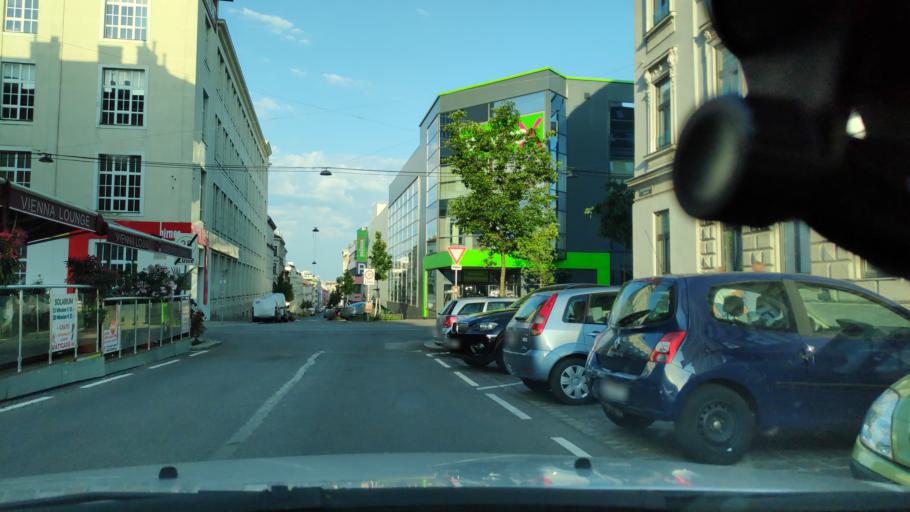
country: AT
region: Vienna
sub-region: Wien Stadt
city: Vienna
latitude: 48.2175
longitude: 16.3195
